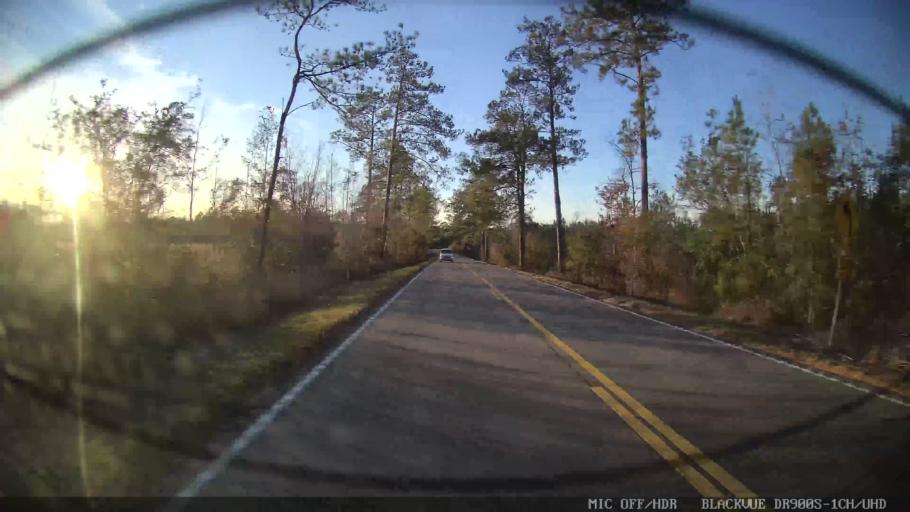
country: US
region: Mississippi
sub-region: Lamar County
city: Lumberton
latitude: 31.0012
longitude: -89.3485
